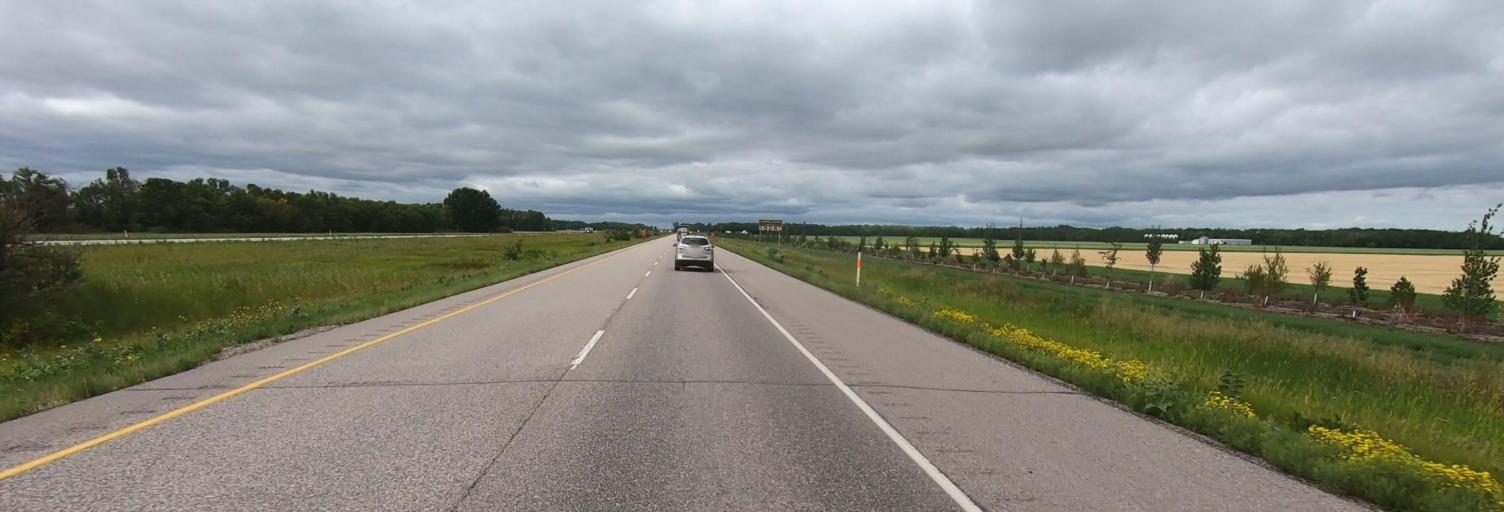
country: CA
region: Manitoba
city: Portage la Prairie
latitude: 49.9638
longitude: -98.0644
